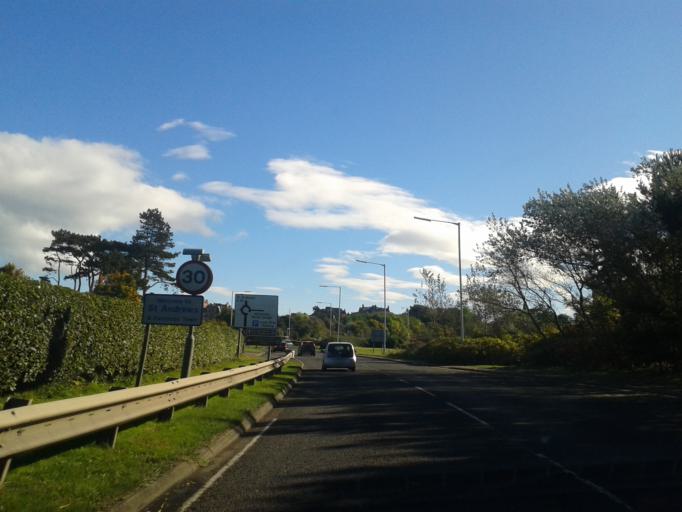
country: GB
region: Scotland
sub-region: Fife
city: Saint Andrews
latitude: 56.3418
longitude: -2.8115
